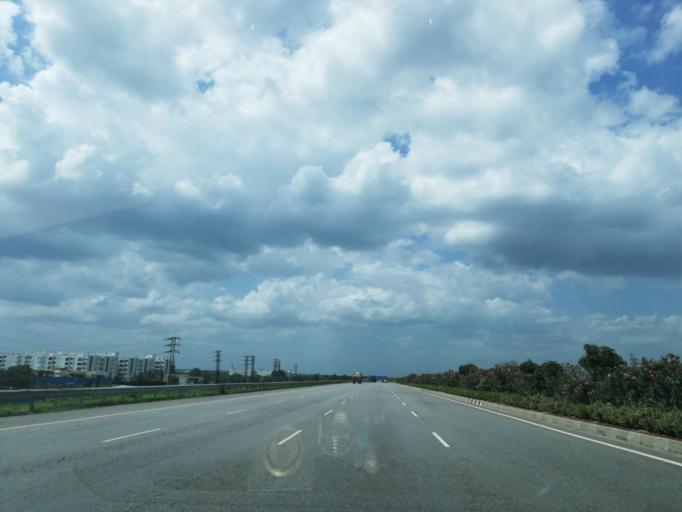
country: IN
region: Telangana
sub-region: Medak
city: Serilingampalle
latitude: 17.4436
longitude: 78.2574
